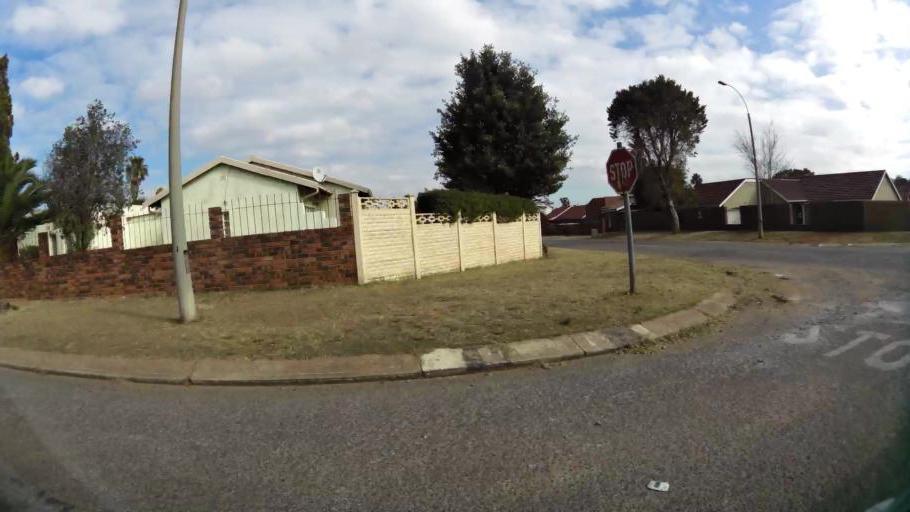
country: ZA
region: Gauteng
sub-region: City of Johannesburg Metropolitan Municipality
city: Roodepoort
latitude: -26.2028
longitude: 27.9158
